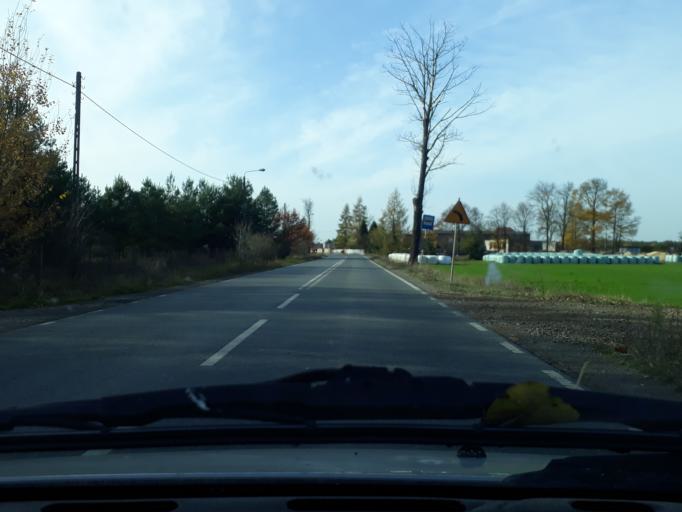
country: PL
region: Silesian Voivodeship
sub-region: Powiat lubliniecki
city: Psary
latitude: 50.5768
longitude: 19.0037
